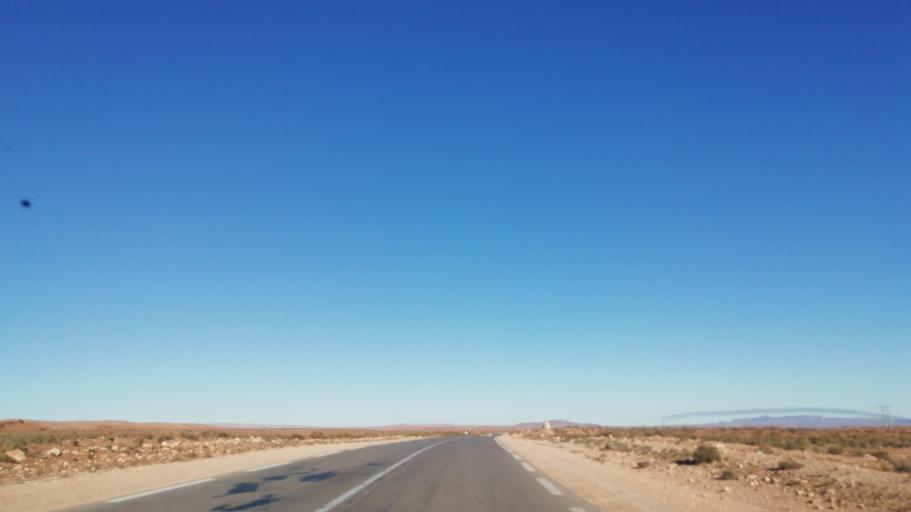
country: DZ
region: El Bayadh
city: El Abiodh Sidi Cheikh
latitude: 33.1328
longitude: 0.2920
